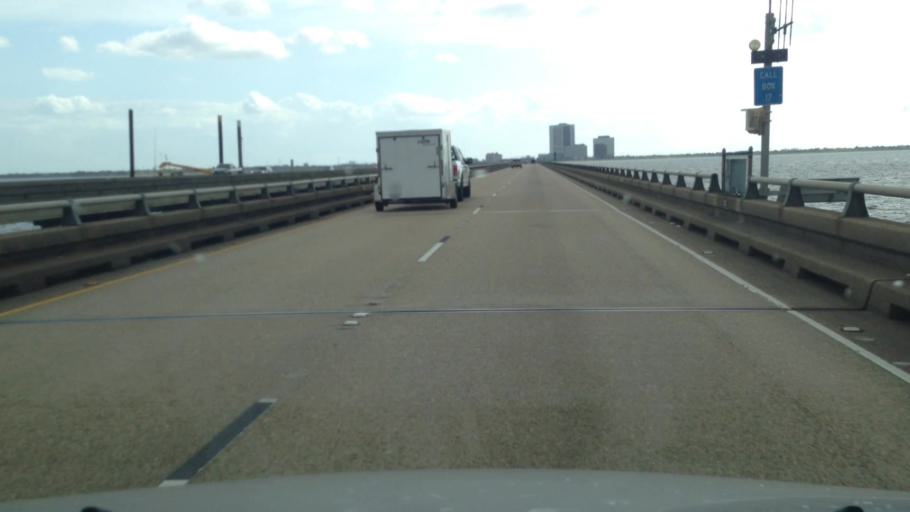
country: US
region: Louisiana
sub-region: Jefferson Parish
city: Metairie
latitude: 30.0461
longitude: -90.1498
